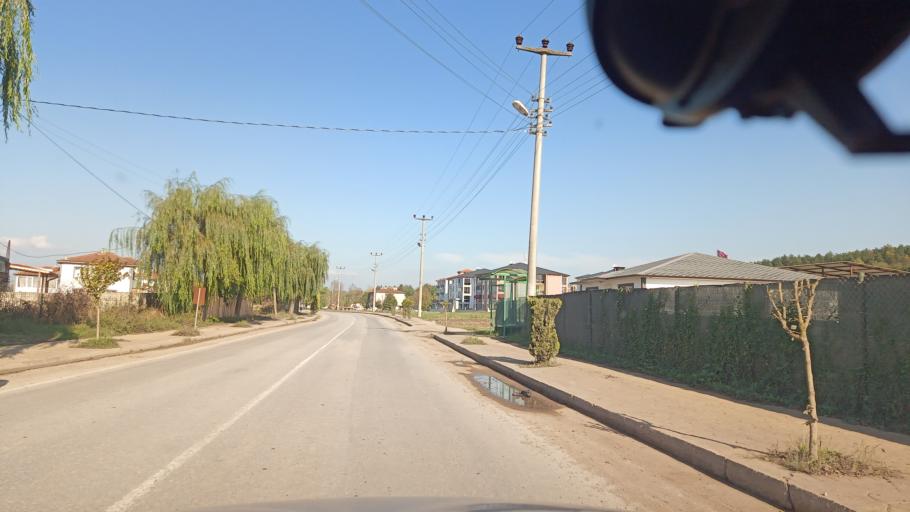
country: TR
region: Sakarya
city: Sogutlu
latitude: 40.8919
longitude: 30.4669
